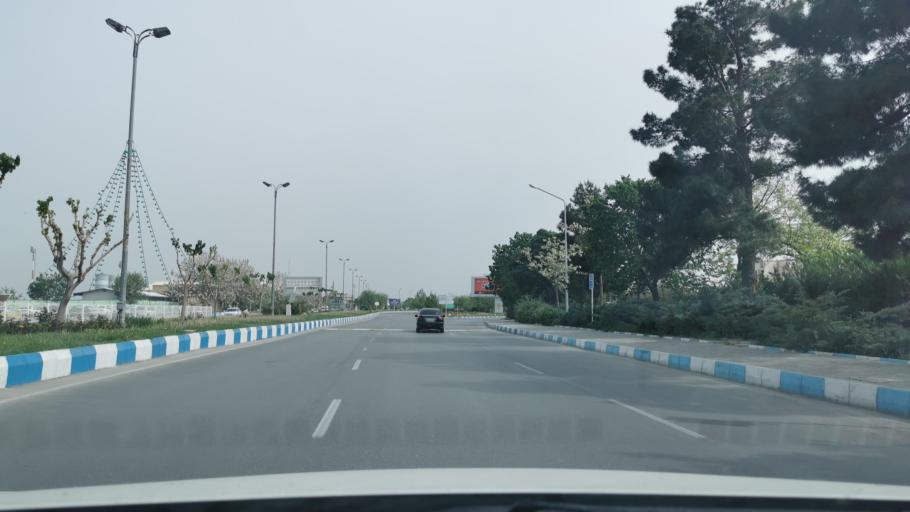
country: IR
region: Razavi Khorasan
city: Mashhad
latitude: 36.2337
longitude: 59.6332
